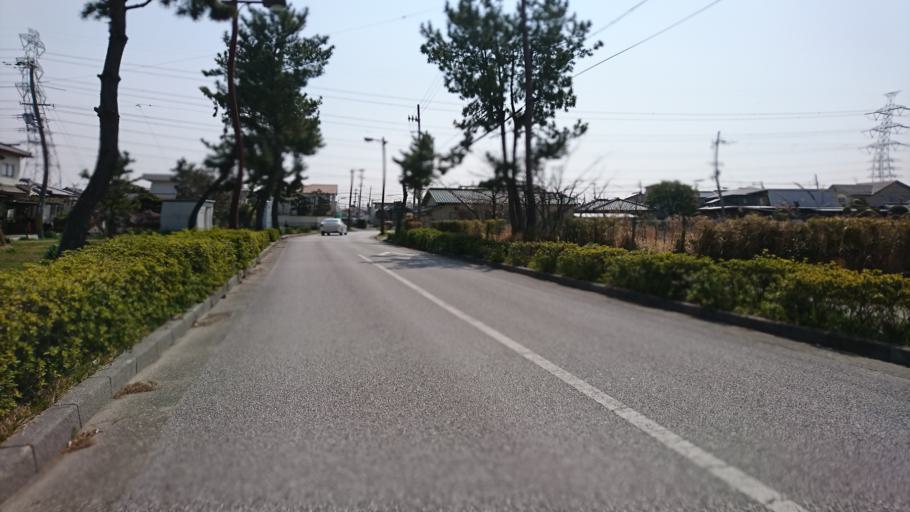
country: JP
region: Hyogo
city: Kakogawacho-honmachi
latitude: 34.7764
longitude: 134.7762
